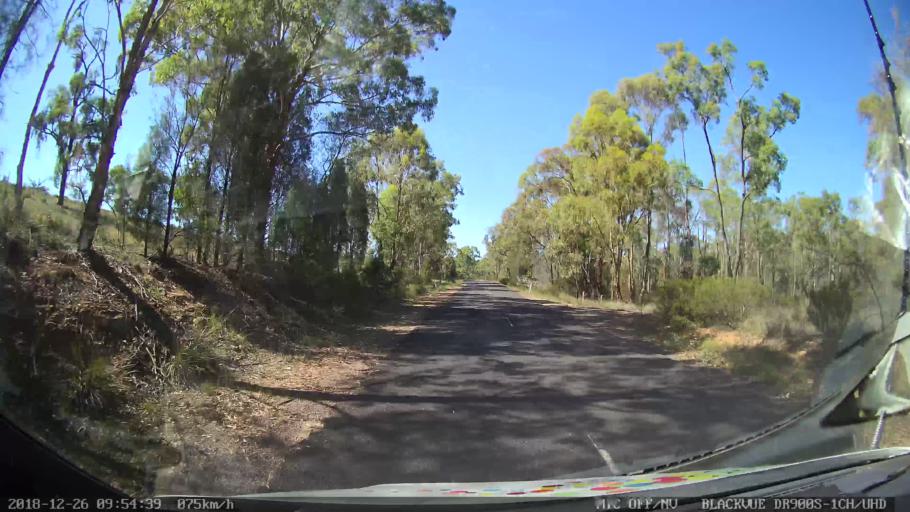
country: AU
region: New South Wales
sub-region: Mid-Western Regional
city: Kandos
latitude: -33.0322
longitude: 150.1618
